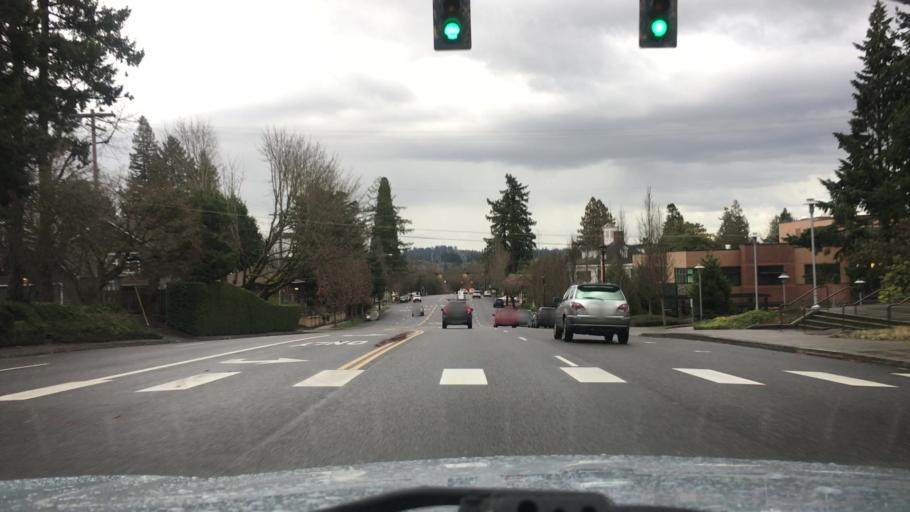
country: US
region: Oregon
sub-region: Clackamas County
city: Lake Oswego
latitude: 45.4203
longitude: -122.6729
